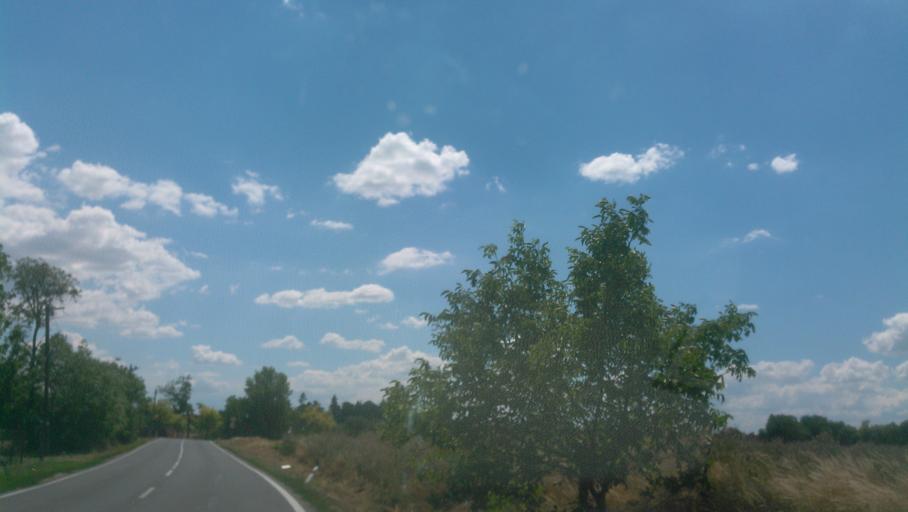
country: SK
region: Trnavsky
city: Vrbove
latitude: 48.5682
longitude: 17.7421
